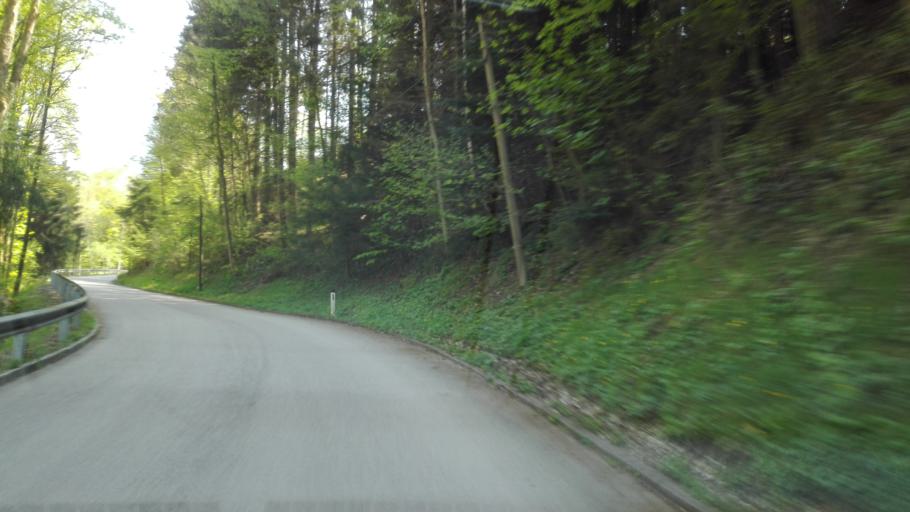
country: AT
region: Upper Austria
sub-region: Politischer Bezirk Rohrbach
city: Atzesberg
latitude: 48.4371
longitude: 13.9171
